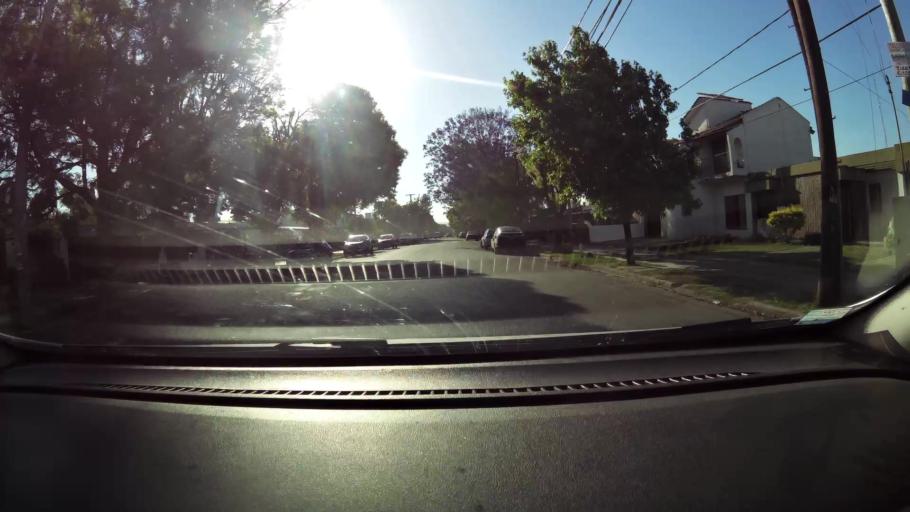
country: AR
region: Cordoba
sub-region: Departamento de Capital
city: Cordoba
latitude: -31.3603
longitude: -64.2175
